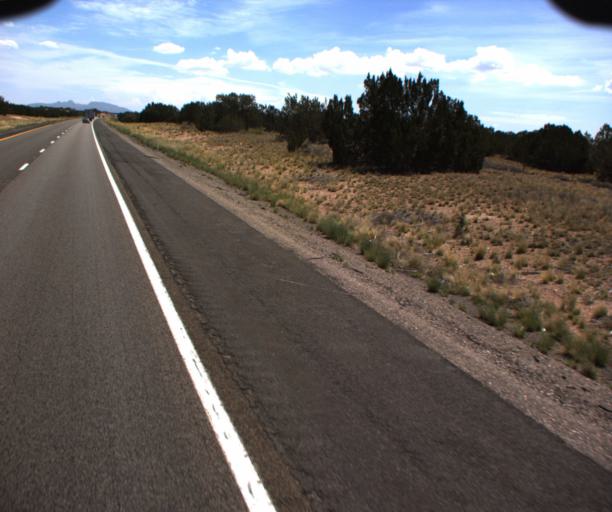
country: US
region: Arizona
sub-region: Mohave County
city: Peach Springs
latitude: 35.3165
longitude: -112.9605
